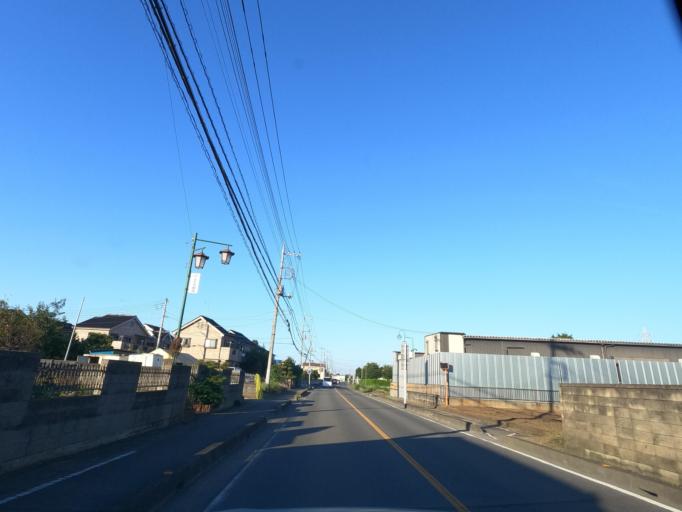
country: JP
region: Saitama
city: Sayama
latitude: 35.9042
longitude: 139.4216
